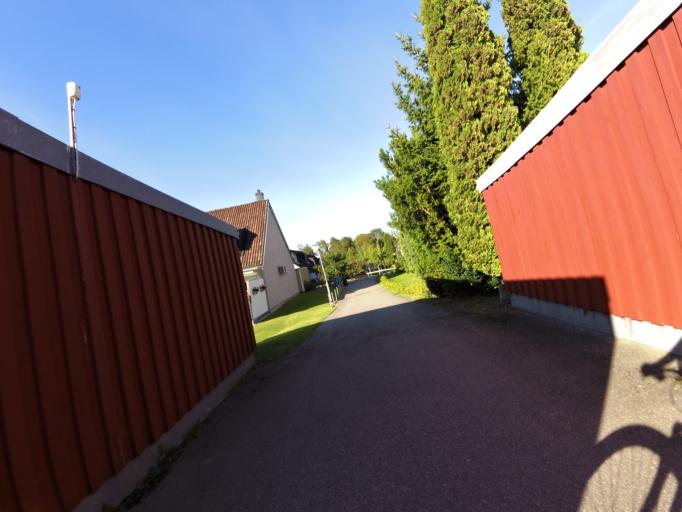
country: SE
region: Gaevleborg
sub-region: Gavle Kommun
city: Gavle
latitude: 60.6481
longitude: 17.1422
